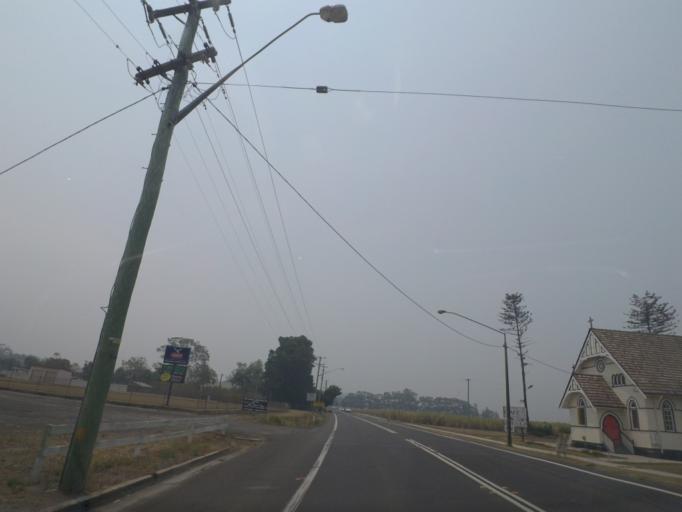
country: AU
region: New South Wales
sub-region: Richmond Valley
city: Evans Head
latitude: -29.0092
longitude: 153.4364
